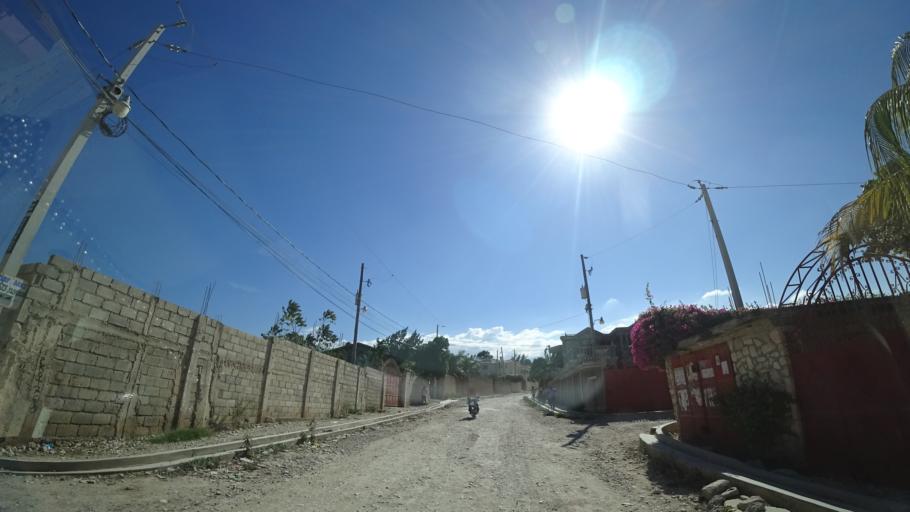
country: HT
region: Ouest
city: Delmas 73
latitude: 18.5518
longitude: -72.2857
